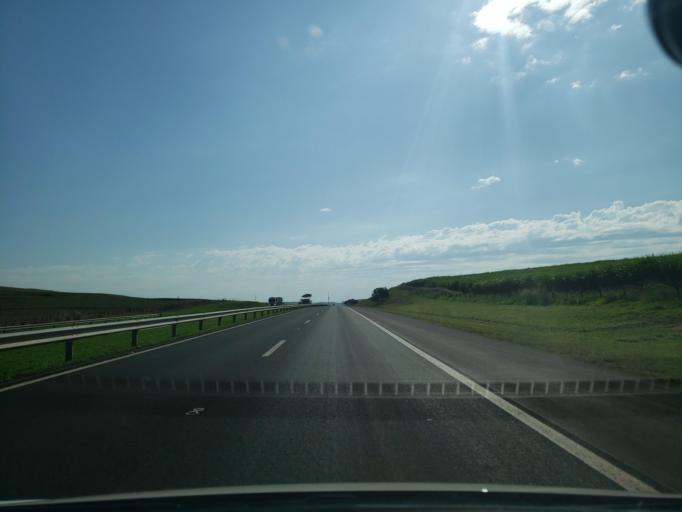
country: BR
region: Sao Paulo
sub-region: Promissao
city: Promissao
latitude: -21.5430
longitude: -49.9674
